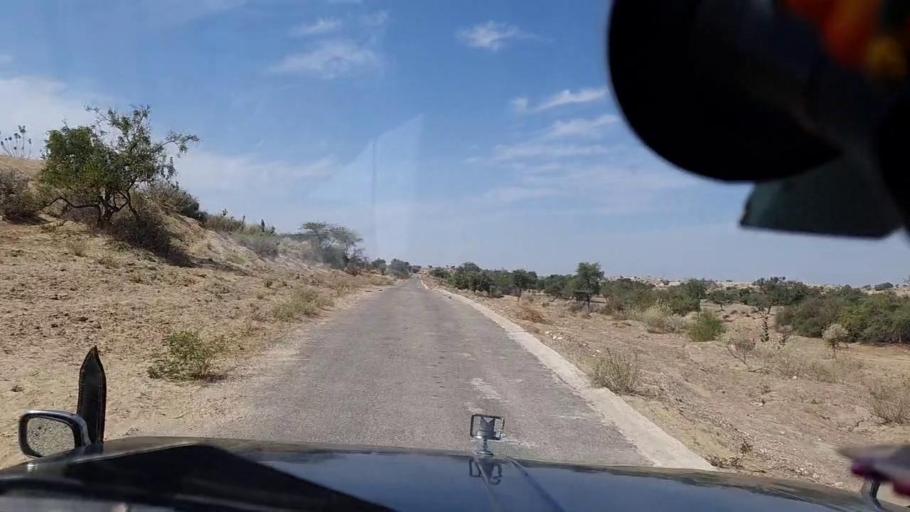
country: PK
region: Sindh
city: Diplo
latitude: 24.3495
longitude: 69.5875
